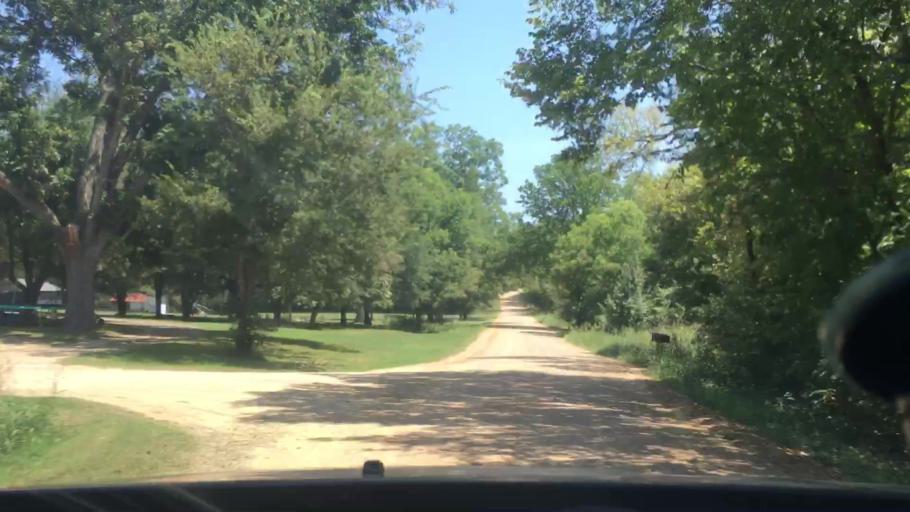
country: US
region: Oklahoma
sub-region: Coal County
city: Coalgate
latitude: 34.3681
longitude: -96.4280
